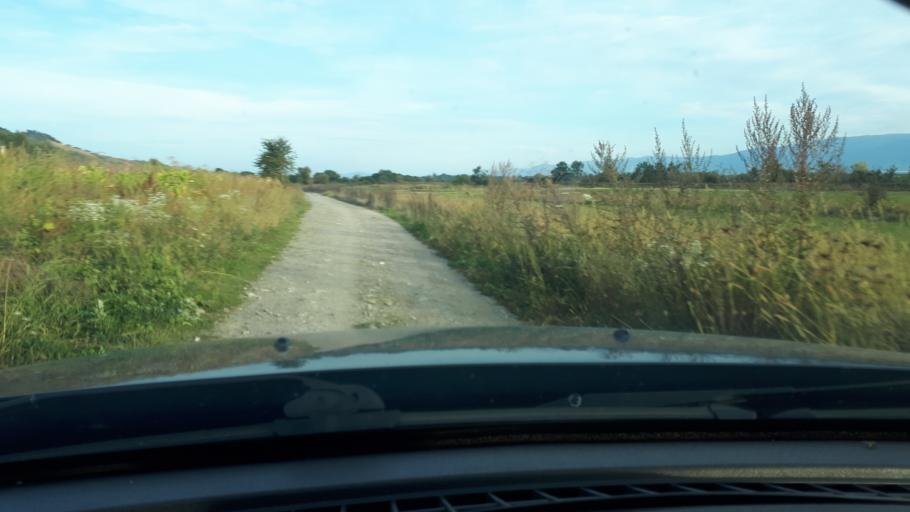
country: RO
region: Brasov
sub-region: Comuna Vistea de Jos
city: Vistea de Jos
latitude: 45.8199
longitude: 24.7751
